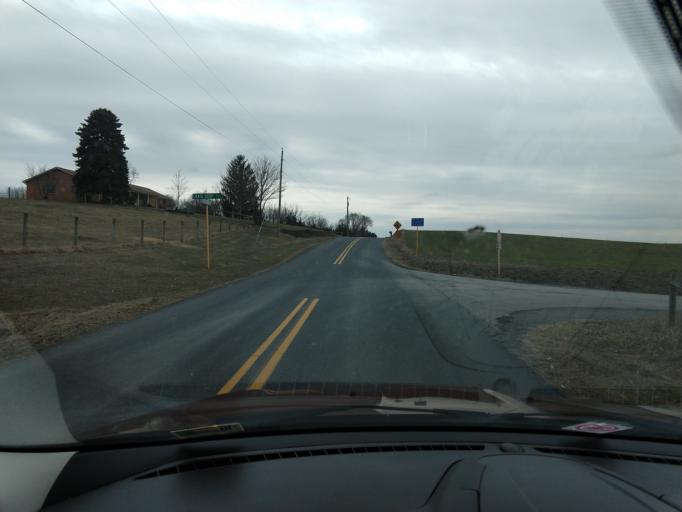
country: US
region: Virginia
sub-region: Rockingham County
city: Grottoes
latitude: 38.2310
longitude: -78.8798
